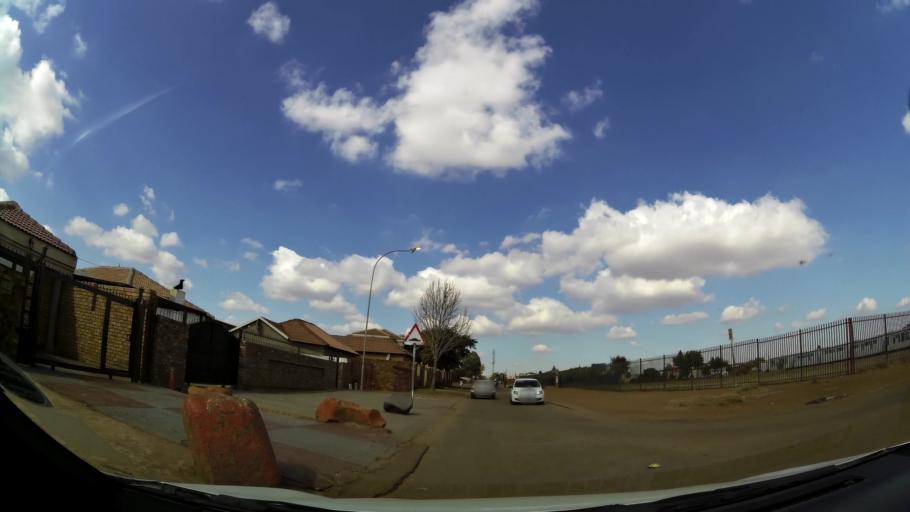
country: ZA
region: Gauteng
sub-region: City of Tshwane Metropolitan Municipality
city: Cullinan
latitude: -25.7020
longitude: 28.4109
